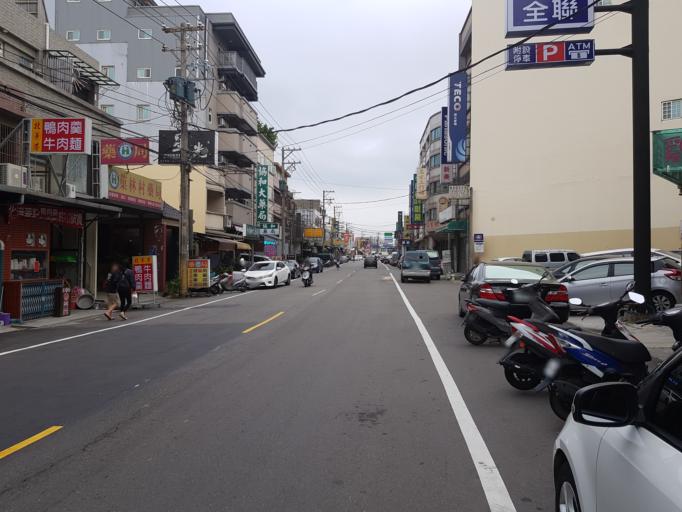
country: TW
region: Taiwan
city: Taoyuan City
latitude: 25.0755
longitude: 121.2584
